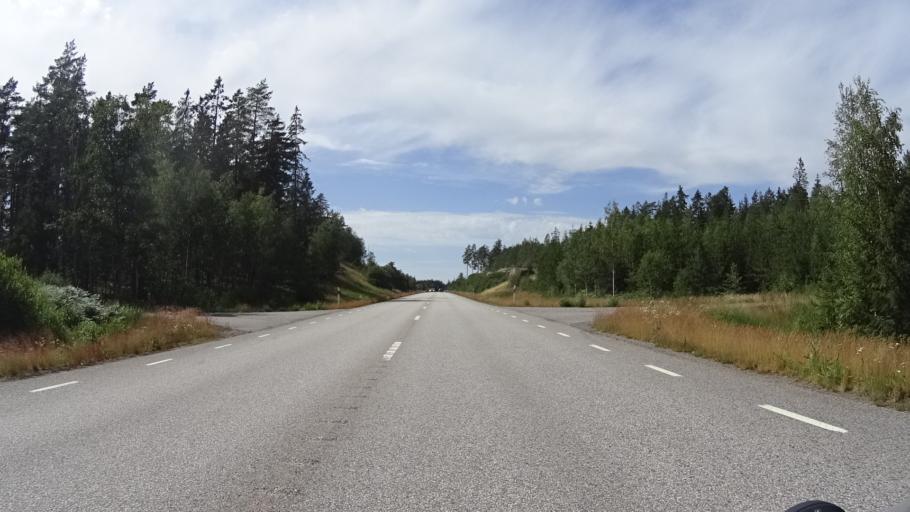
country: SE
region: Kalmar
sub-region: Vasterviks Kommun
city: Overum
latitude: 57.9601
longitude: 16.3647
